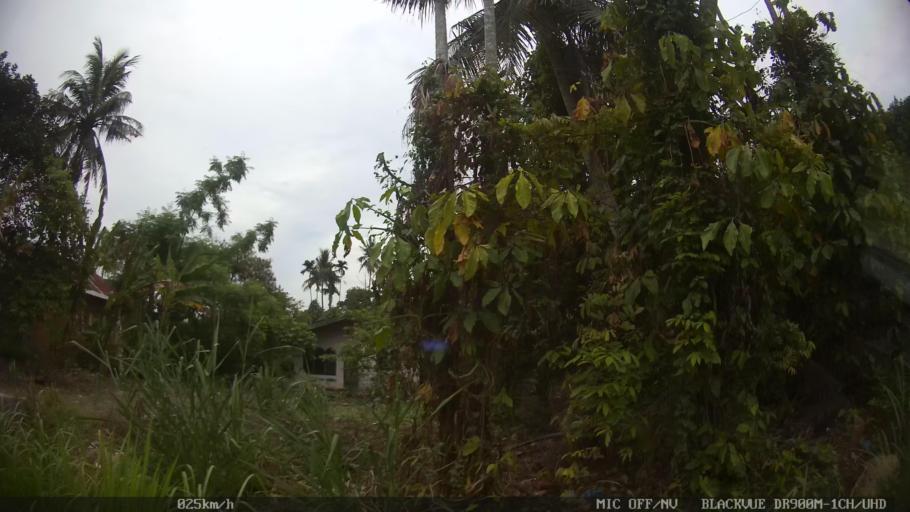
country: ID
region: North Sumatra
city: Binjai
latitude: 3.6188
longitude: 98.5544
